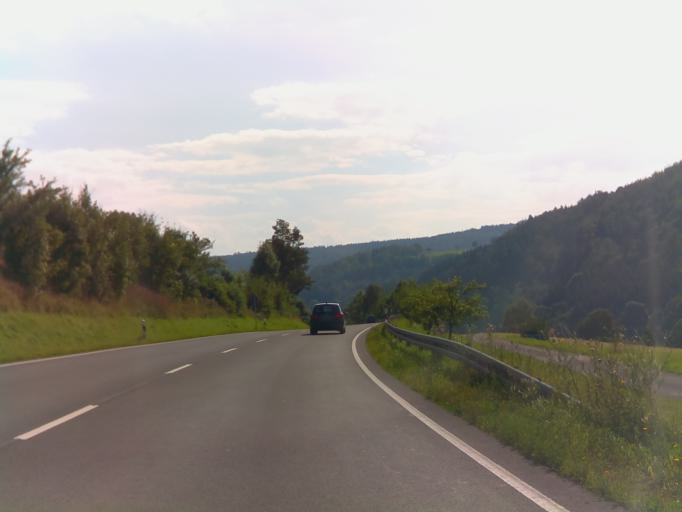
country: DE
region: Bavaria
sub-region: Regierungsbezirk Unterfranken
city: Wildflecken
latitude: 50.3607
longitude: 9.8913
